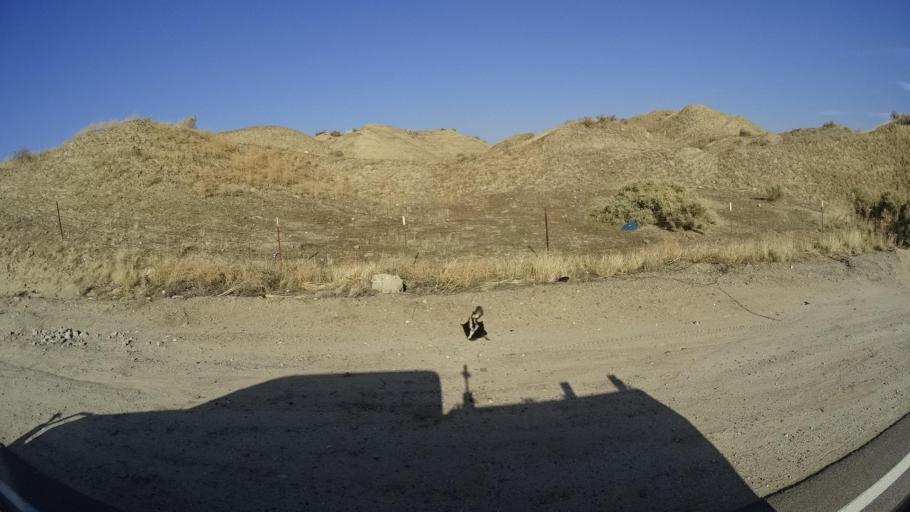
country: US
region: California
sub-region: Kern County
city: Oildale
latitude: 35.4514
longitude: -118.9302
